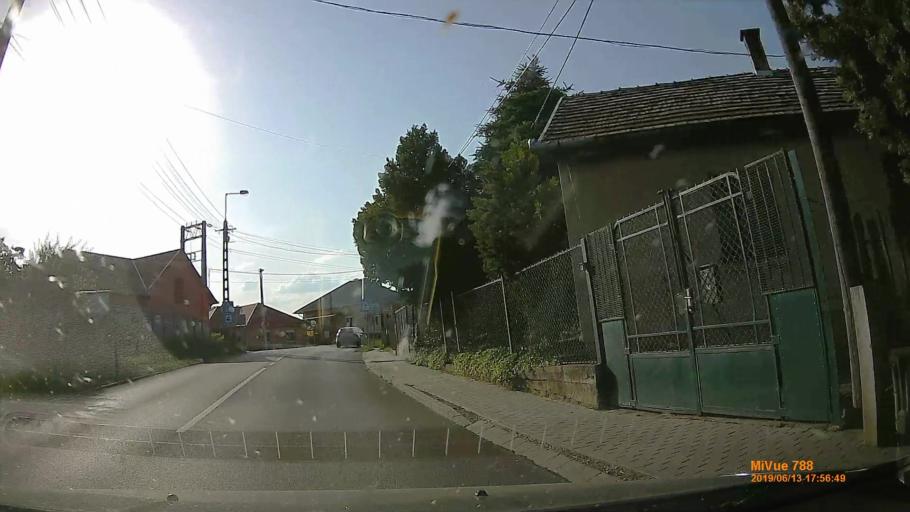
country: HU
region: Pest
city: Ecser
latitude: 47.4429
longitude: 19.3405
